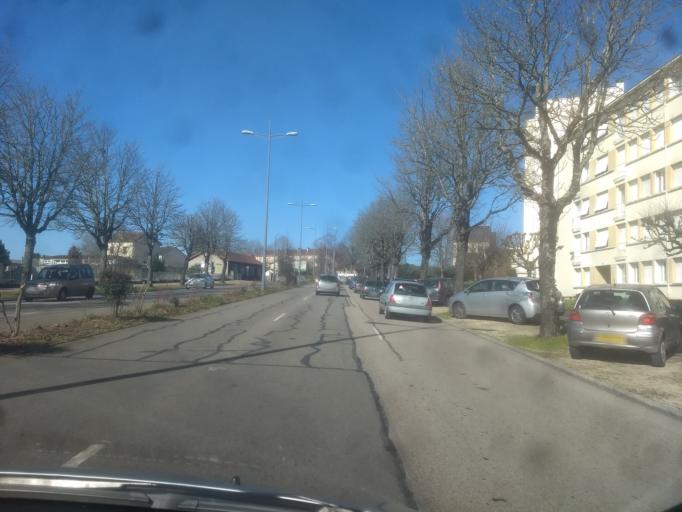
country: FR
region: Limousin
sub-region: Departement de la Haute-Vienne
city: Isle
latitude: 45.8232
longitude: 1.2272
